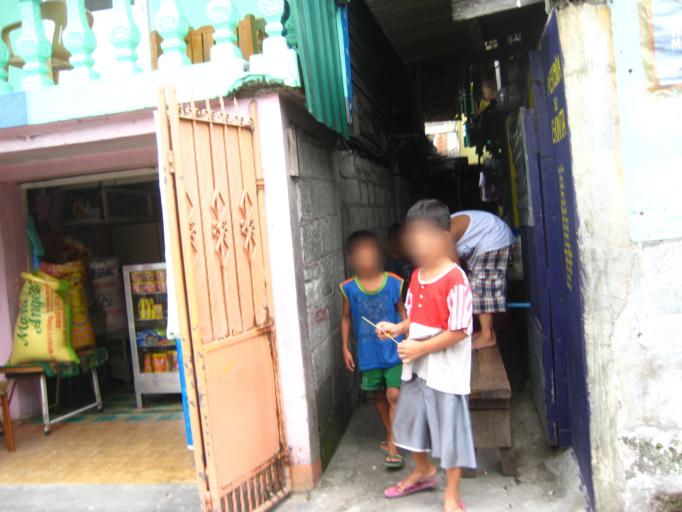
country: PH
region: Calabarzon
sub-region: Province of Rizal
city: Pateros
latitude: 14.5408
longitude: 121.0701
